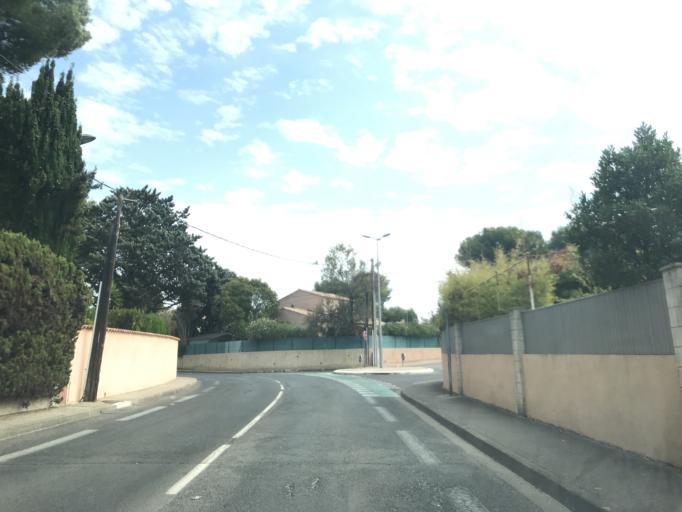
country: FR
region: Provence-Alpes-Cote d'Azur
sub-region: Departement du Var
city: Six-Fours-les-Plages
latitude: 43.0878
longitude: 5.8177
